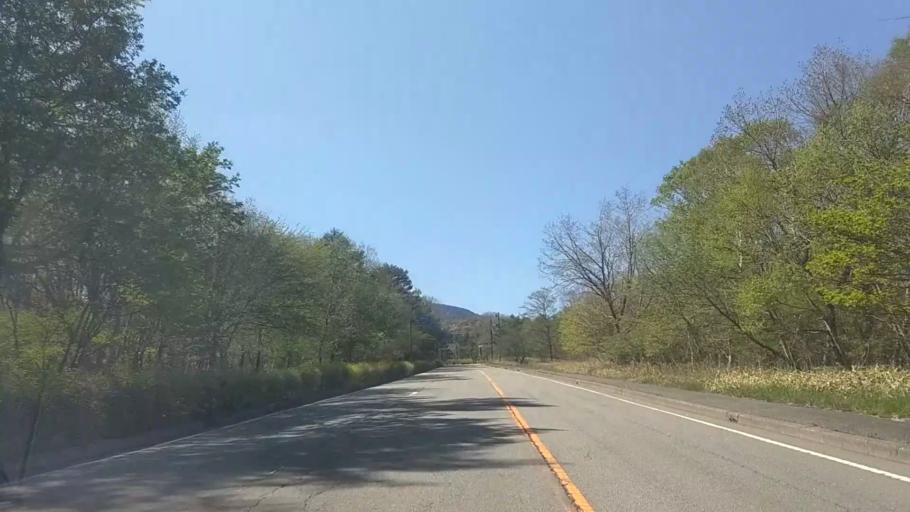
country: JP
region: Yamanashi
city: Nirasaki
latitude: 35.9330
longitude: 138.4259
